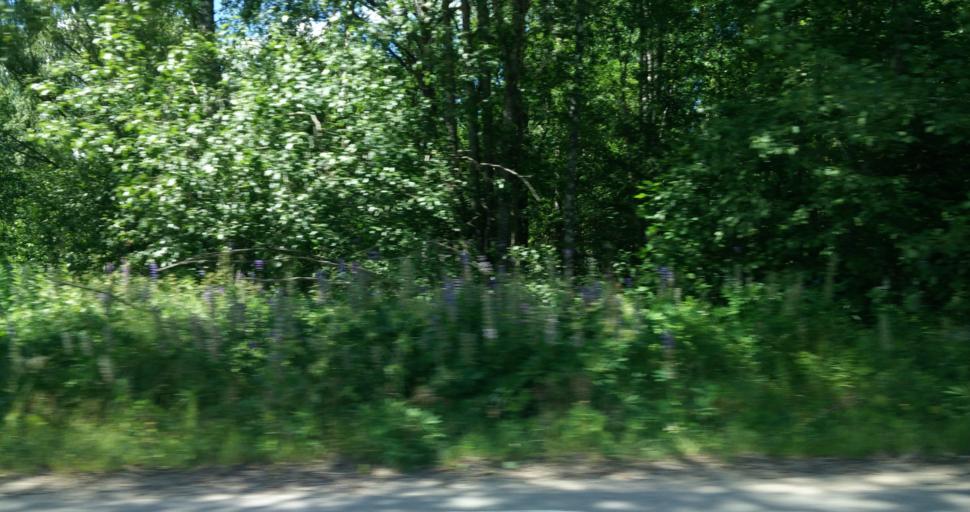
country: SE
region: Vaermland
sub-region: Hagfors Kommun
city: Hagfors
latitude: 60.0310
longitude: 13.6257
